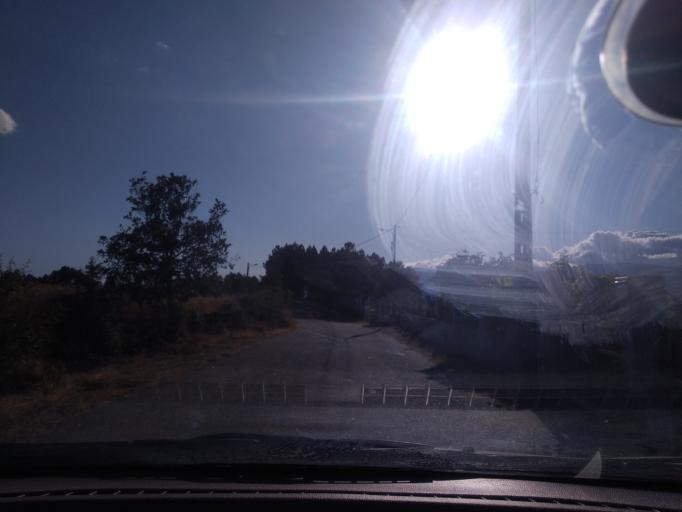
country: PT
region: Castelo Branco
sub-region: Covilha
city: Teixoso
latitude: 40.2587
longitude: -7.3940
